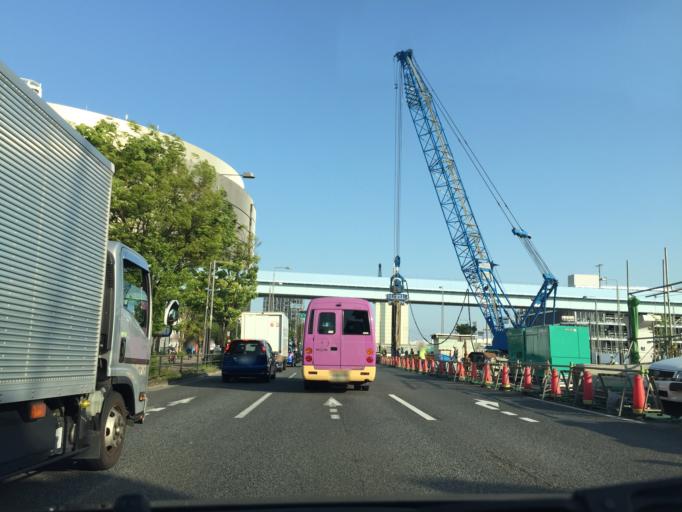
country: JP
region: Tokyo
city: Urayasu
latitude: 35.6488
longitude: 139.7886
